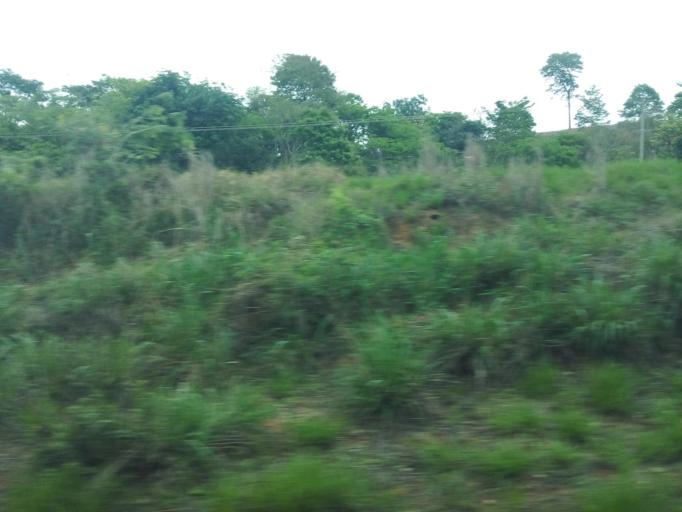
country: BR
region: Minas Gerais
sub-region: Ipaba
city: Ipaba
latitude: -19.4264
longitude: -42.4322
